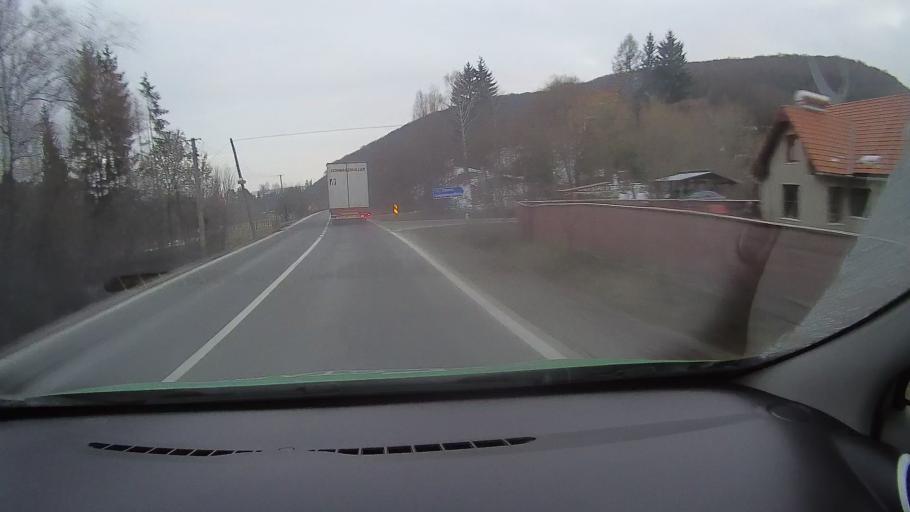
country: RO
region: Harghita
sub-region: Municipiul Odorheiu Secuiesc
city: Odorheiu Secuiesc
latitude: 46.3359
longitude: 25.2704
